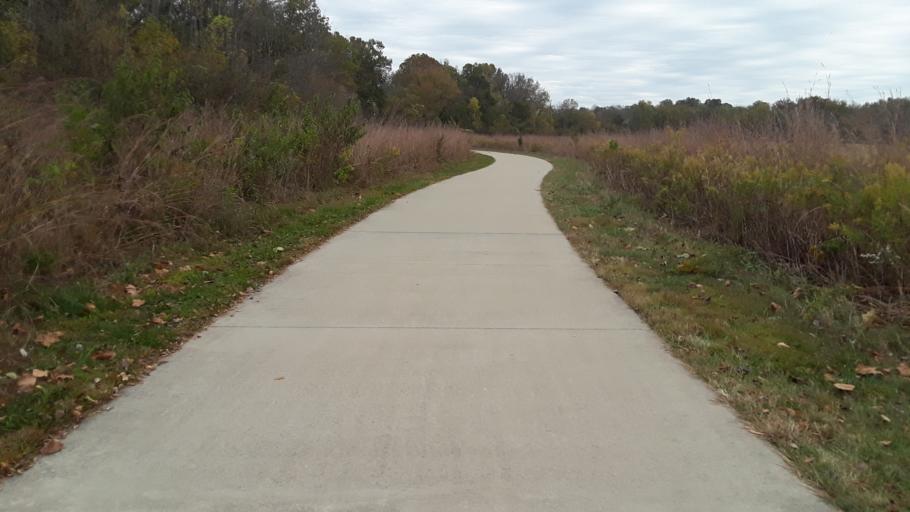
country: US
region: Kentucky
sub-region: Jefferson County
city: Middletown
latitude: 38.2037
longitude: -85.4776
